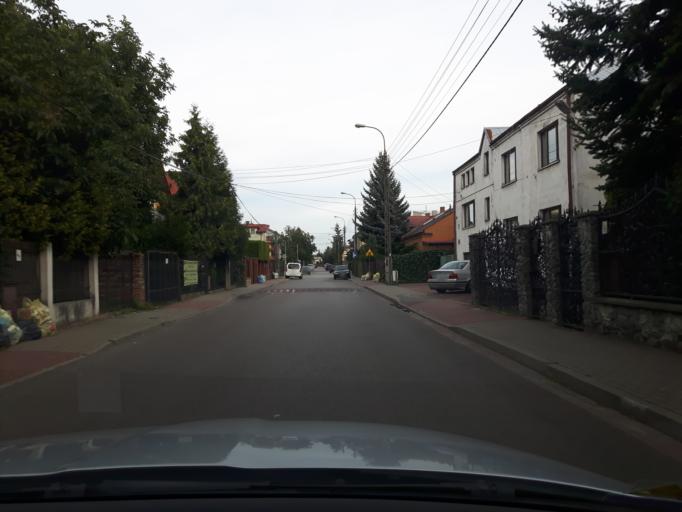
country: PL
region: Masovian Voivodeship
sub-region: Warszawa
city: Targowek
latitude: 52.2781
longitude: 21.0584
